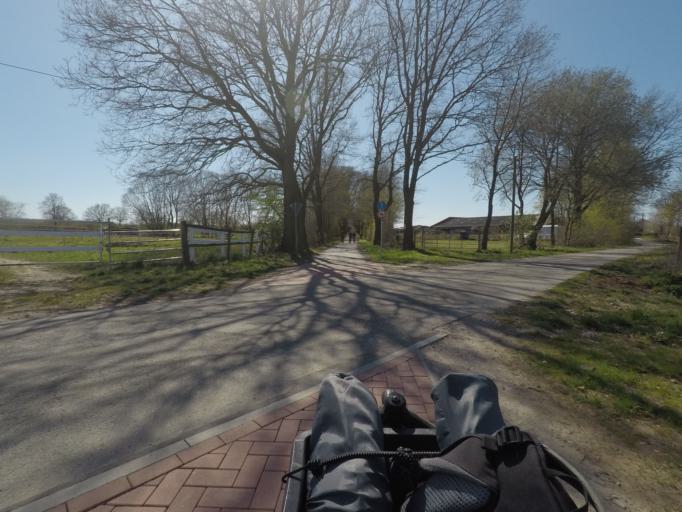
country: DE
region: Schleswig-Holstein
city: Siek
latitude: 53.6065
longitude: 10.2826
